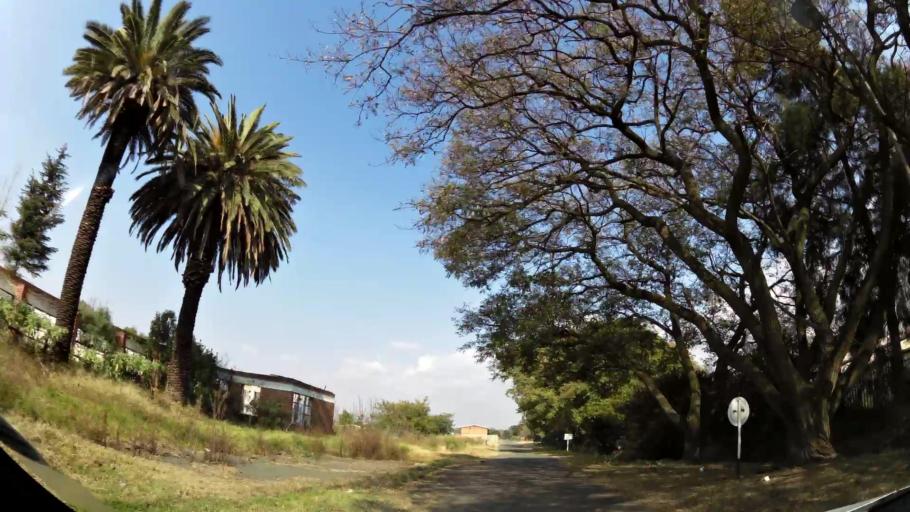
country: ZA
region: Gauteng
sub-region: Ekurhuleni Metropolitan Municipality
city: Boksburg
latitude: -26.1613
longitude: 28.2067
